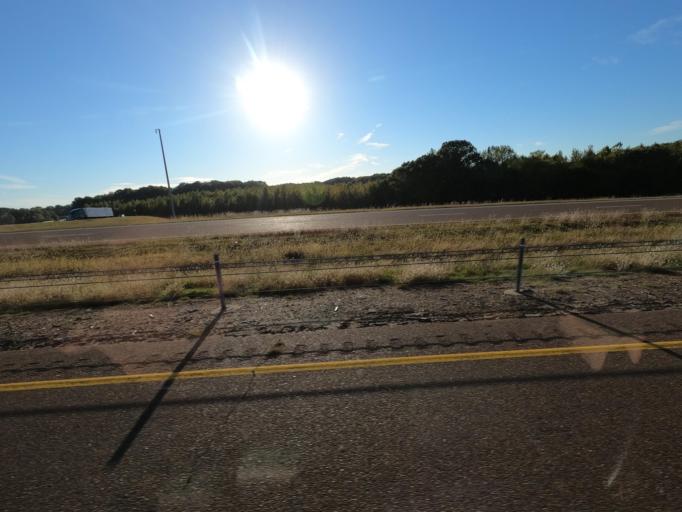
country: US
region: Tennessee
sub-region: Shelby County
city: Arlington
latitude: 35.2583
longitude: -89.6780
